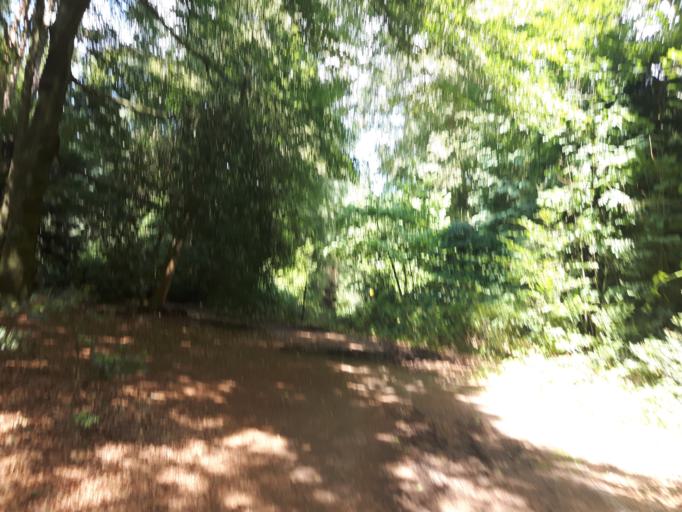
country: NL
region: Overijssel
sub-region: Gemeente Haaksbergen
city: Haaksbergen
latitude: 52.1659
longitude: 6.7608
